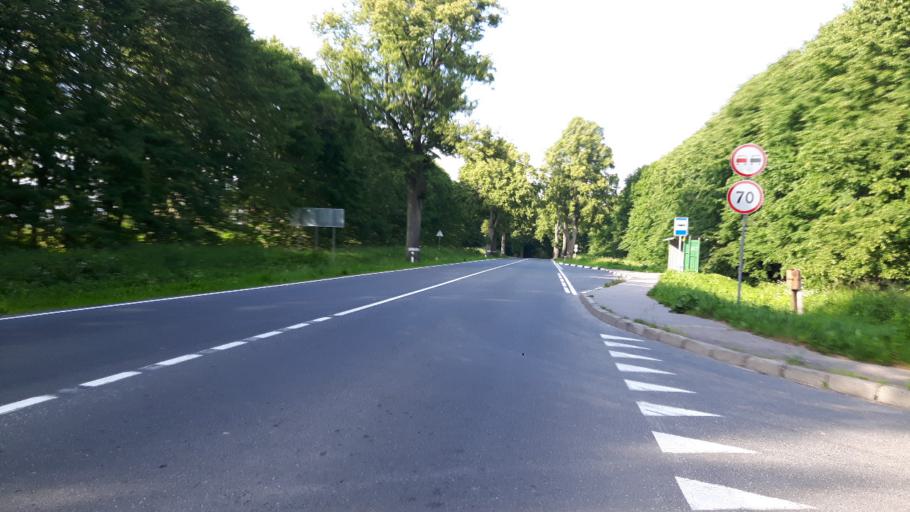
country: RU
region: Kaliningrad
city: Ladushkin
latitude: 54.5253
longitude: 20.1189
